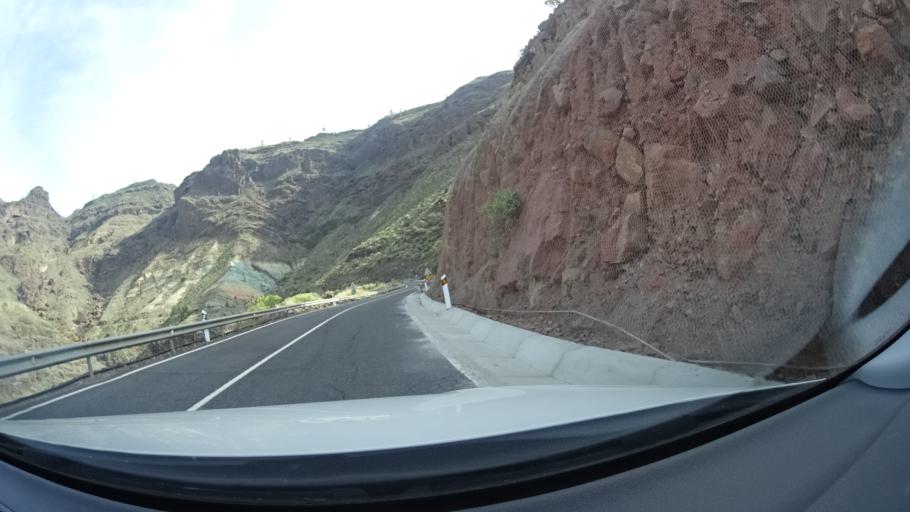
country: ES
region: Canary Islands
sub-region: Provincia de Las Palmas
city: Mogan
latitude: 27.9182
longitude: -15.7288
